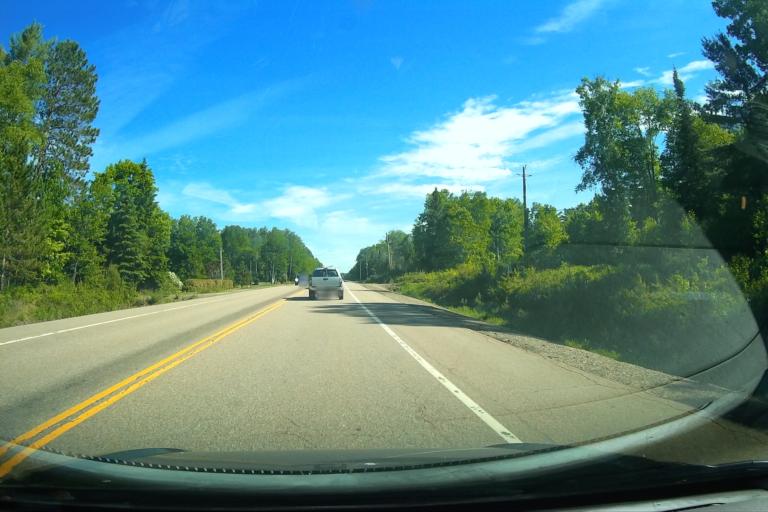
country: CA
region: Ontario
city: Deep River
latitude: 46.2060
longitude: -77.8843
